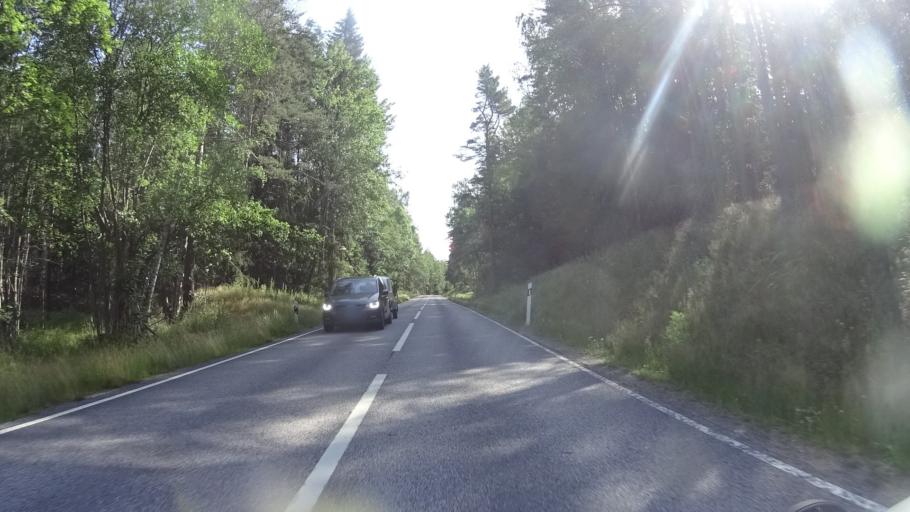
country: SE
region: Kalmar
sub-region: Vasterviks Kommun
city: Overum
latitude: 58.0787
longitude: 16.1726
